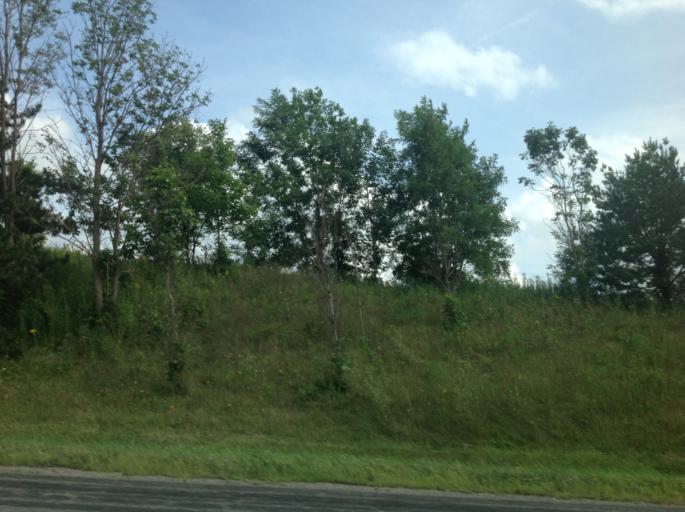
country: US
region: Ohio
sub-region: Richland County
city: Lincoln Heights
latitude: 40.7608
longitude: -82.4299
